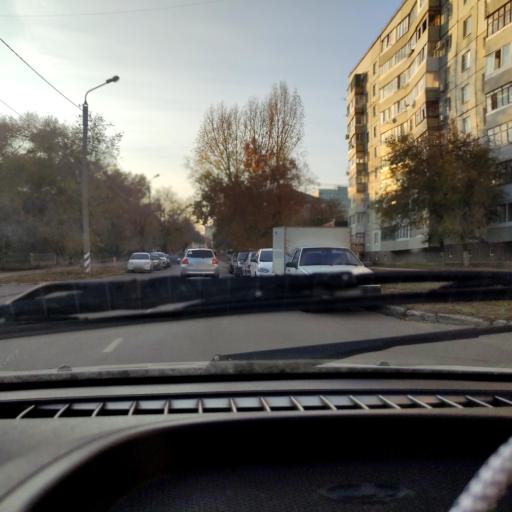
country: RU
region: Samara
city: Zhigulevsk
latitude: 53.4763
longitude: 49.4784
